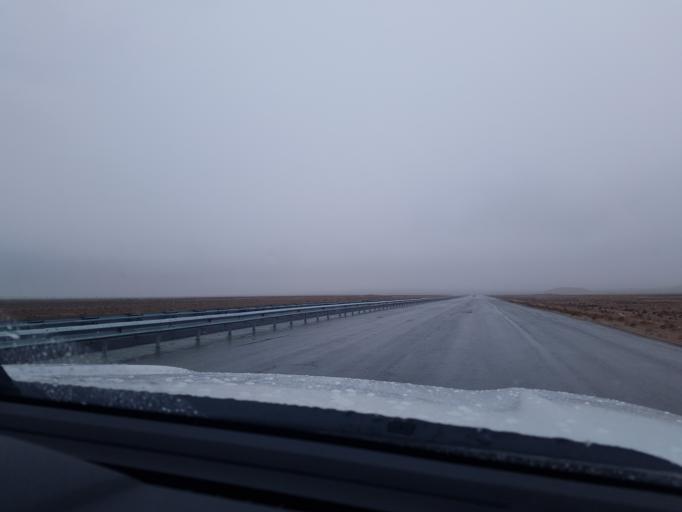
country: TM
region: Balkan
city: Turkmenbasy
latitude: 40.0376
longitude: 53.6354
